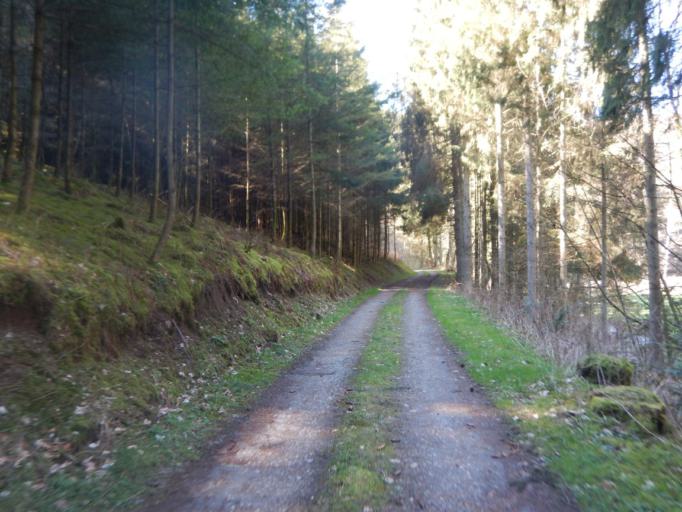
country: LU
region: Diekirch
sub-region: Canton de Wiltz
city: Eschweiler
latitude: 49.9718
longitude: 5.9697
